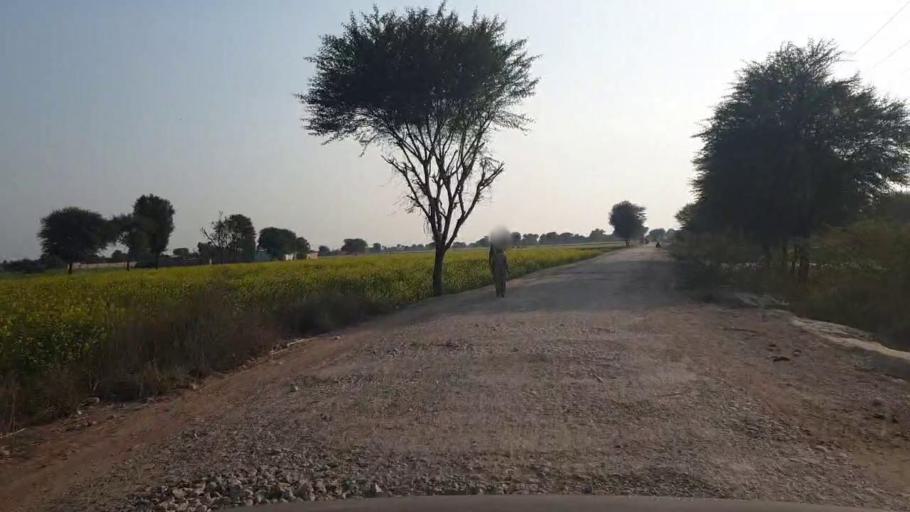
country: PK
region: Sindh
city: Bhit Shah
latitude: 25.7783
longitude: 68.4679
